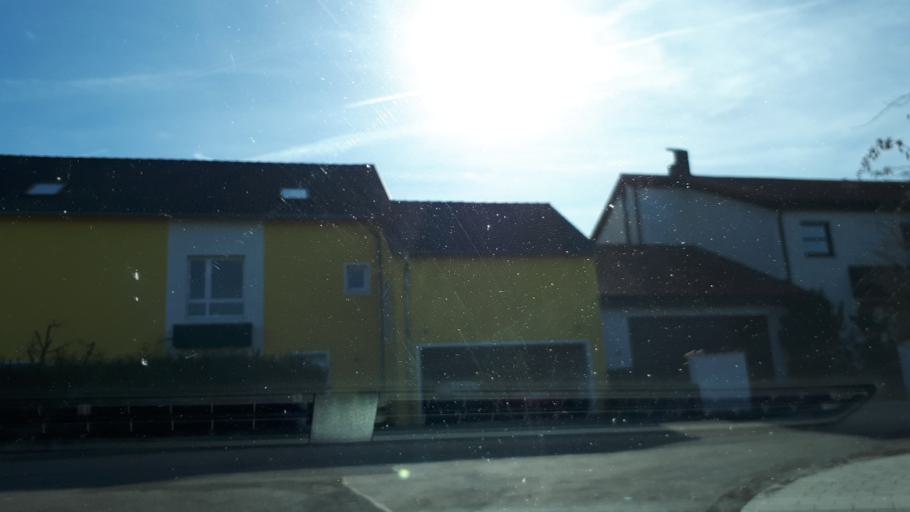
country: DE
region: Bavaria
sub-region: Upper Palatinate
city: Pentling
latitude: 48.9801
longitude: 12.0546
